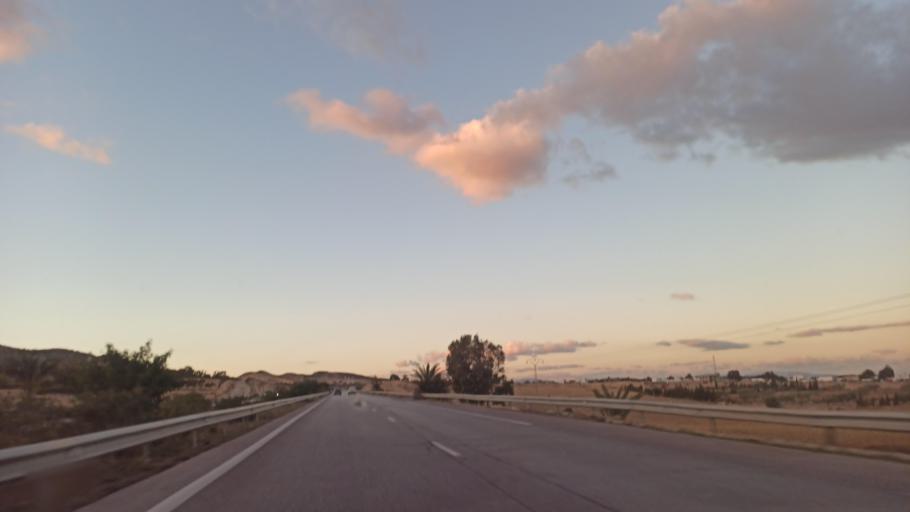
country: TN
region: Susah
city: Harqalah
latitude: 36.2239
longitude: 10.4161
